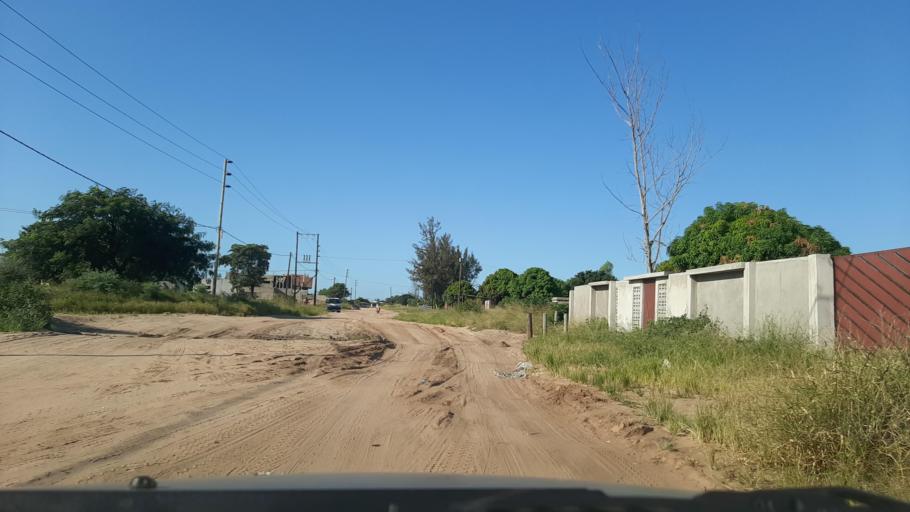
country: MZ
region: Maputo City
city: Maputo
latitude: -25.7613
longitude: 32.5485
